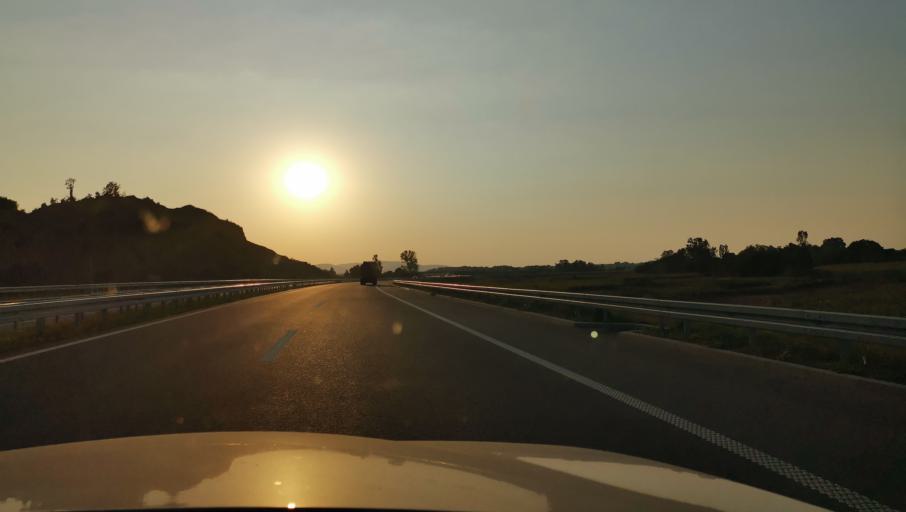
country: RS
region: Central Serbia
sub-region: Kolubarski Okrug
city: Lajkovac
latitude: 44.3439
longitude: 20.1878
